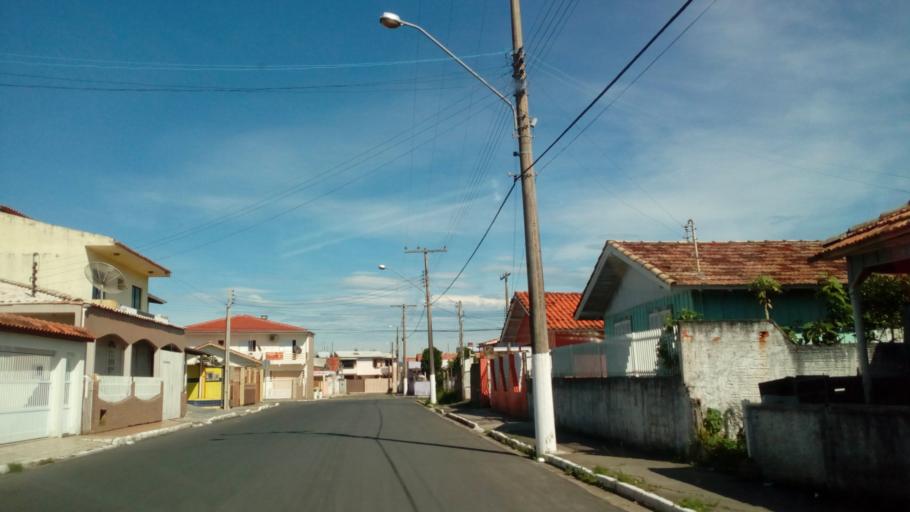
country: BR
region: Santa Catarina
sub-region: Laguna
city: Laguna
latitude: -28.4956
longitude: -48.7770
